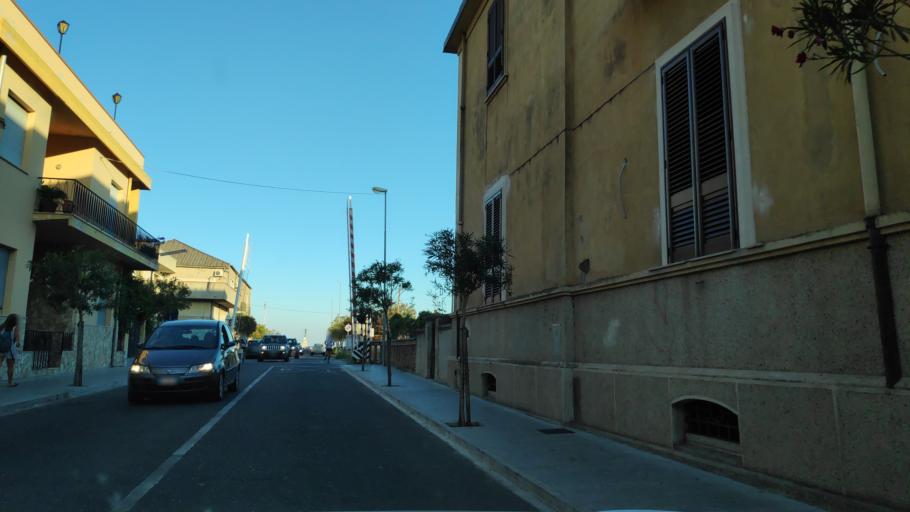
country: IT
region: Calabria
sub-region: Provincia di Reggio Calabria
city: Locri
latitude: 38.2354
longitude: 16.2663
